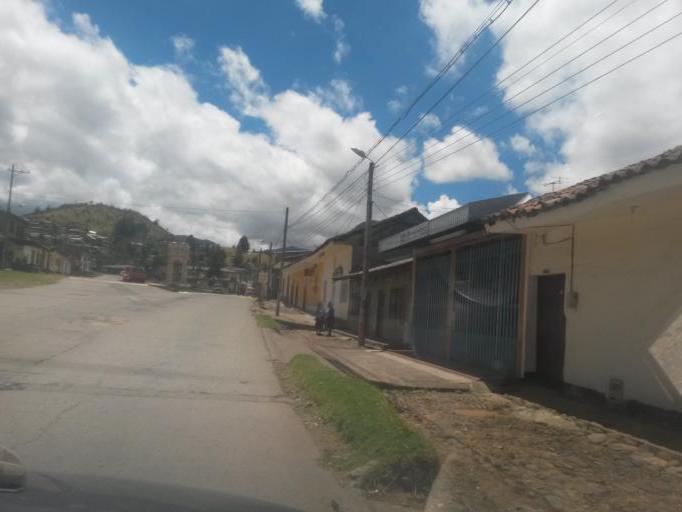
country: CO
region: Cauca
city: Silvia
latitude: 2.6152
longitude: -76.3736
